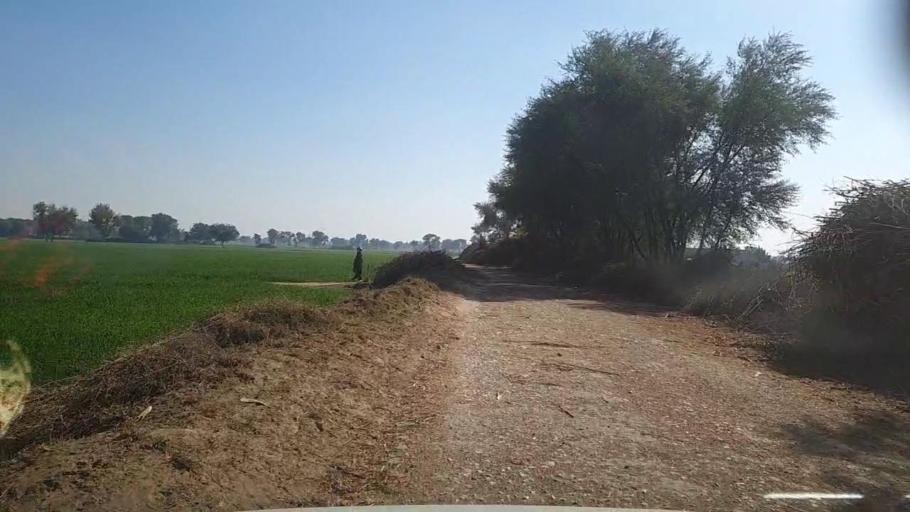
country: PK
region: Sindh
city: Khairpur
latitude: 28.0479
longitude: 69.8182
